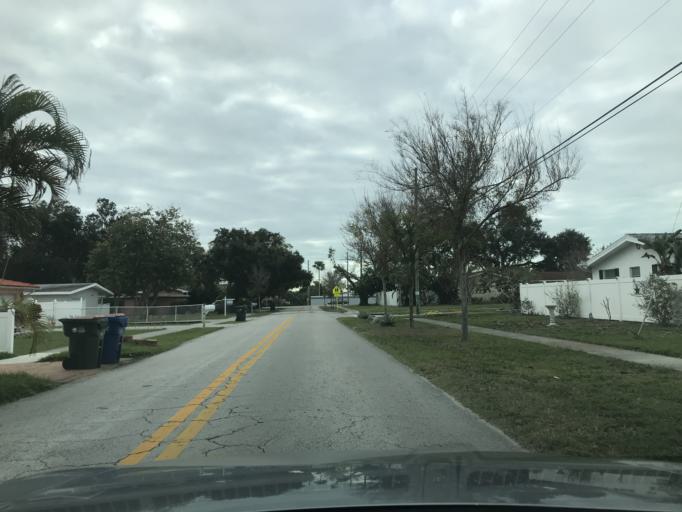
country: US
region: Florida
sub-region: Pinellas County
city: Largo
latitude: 27.9290
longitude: -82.7834
